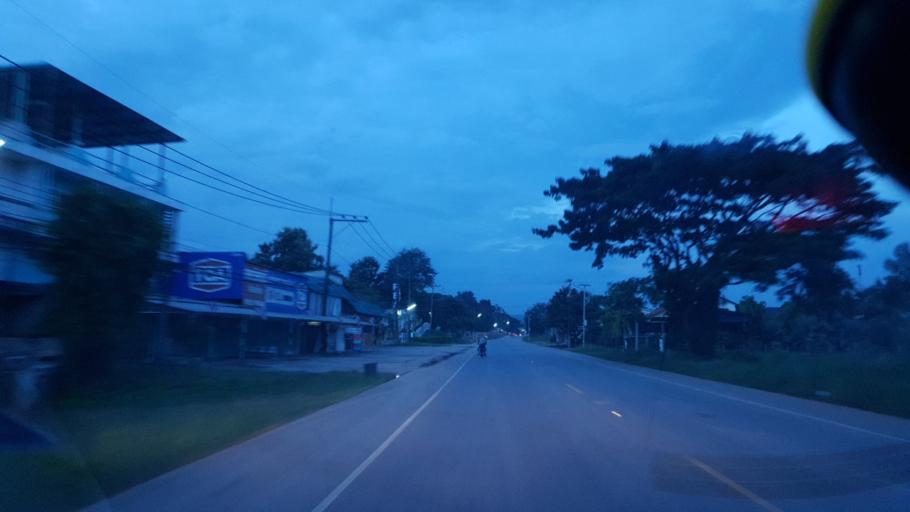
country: TH
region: Chiang Rai
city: Wiang Chiang Rung
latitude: 19.9983
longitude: 100.0394
